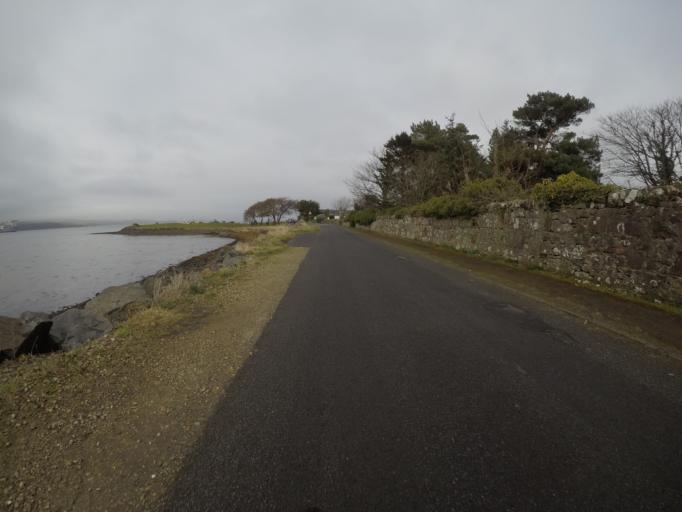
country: GB
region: Scotland
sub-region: North Ayrshire
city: Fairlie
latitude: 55.7505
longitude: -4.8574
